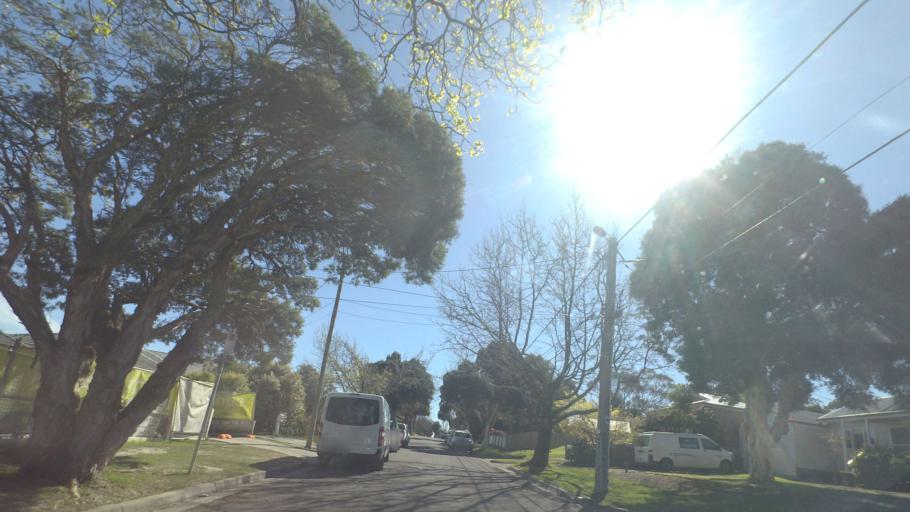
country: AU
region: Victoria
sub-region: Maroondah
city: Ringwood East
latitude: -37.8166
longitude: 145.2496
